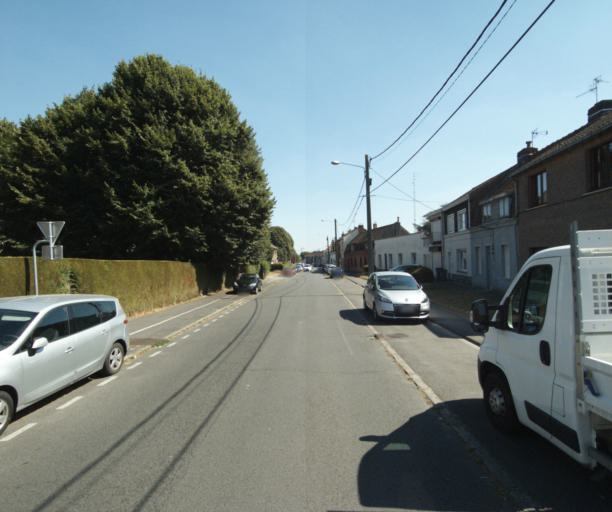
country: FR
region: Nord-Pas-de-Calais
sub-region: Departement du Nord
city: Wattrelos
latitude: 50.7029
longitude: 3.1992
